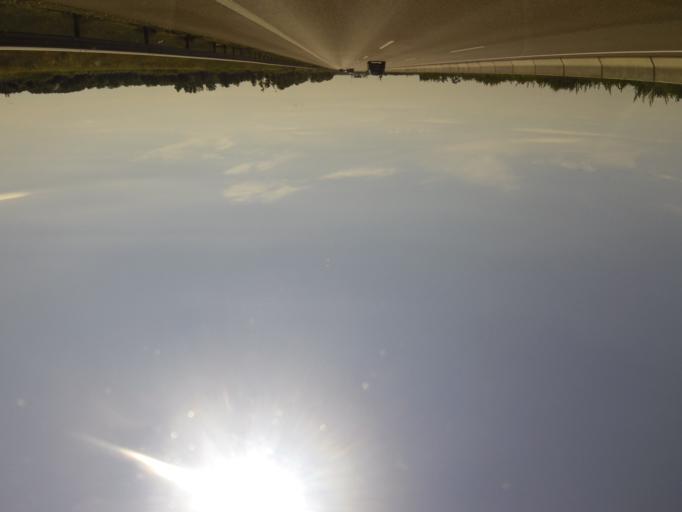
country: DE
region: Bavaria
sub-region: Swabia
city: Nersingen
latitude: 48.4609
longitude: 10.1598
